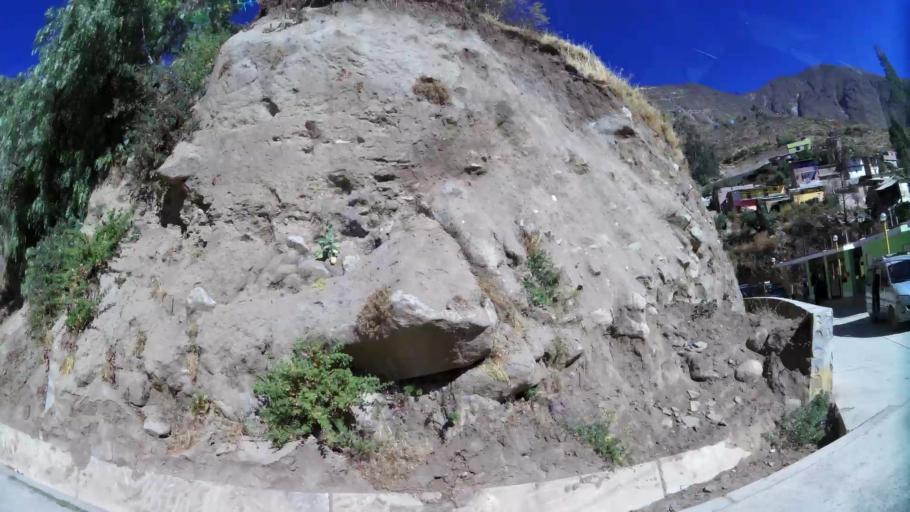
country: PE
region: Huancavelica
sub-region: Huaytara
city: Quito-Arma
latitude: -13.6044
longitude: -75.3515
